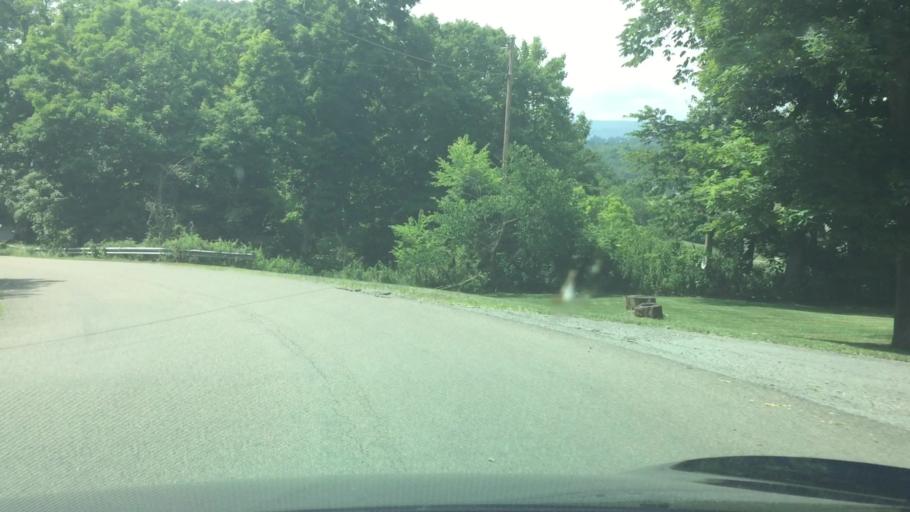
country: US
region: Virginia
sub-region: Wythe County
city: Wytheville
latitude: 36.9292
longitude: -81.0667
